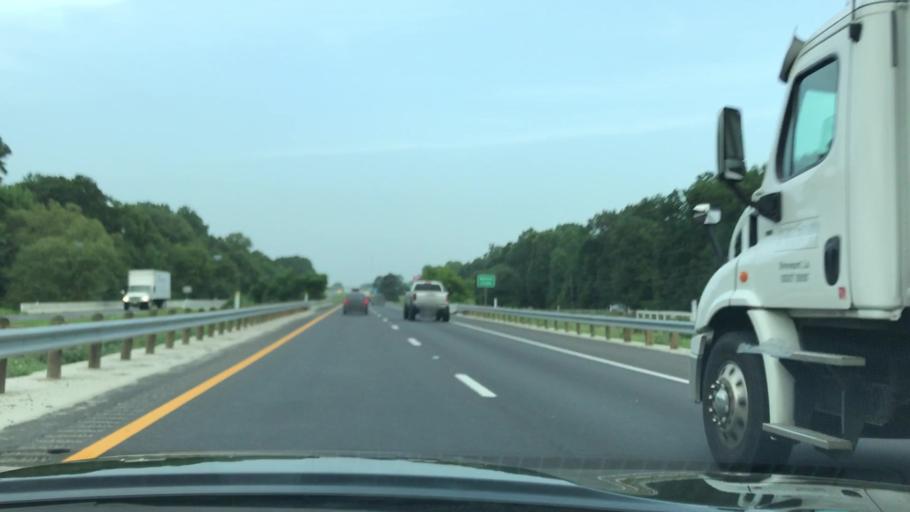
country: US
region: Texas
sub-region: Harrison County
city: Hallsville
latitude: 32.4625
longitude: -94.6510
